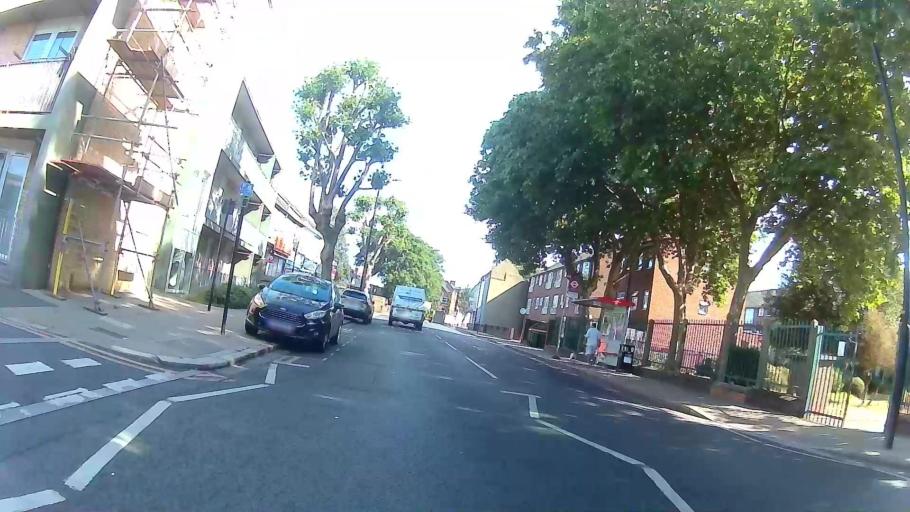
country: GB
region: England
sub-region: Greater London
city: East Ham
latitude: 51.5268
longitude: 0.0240
